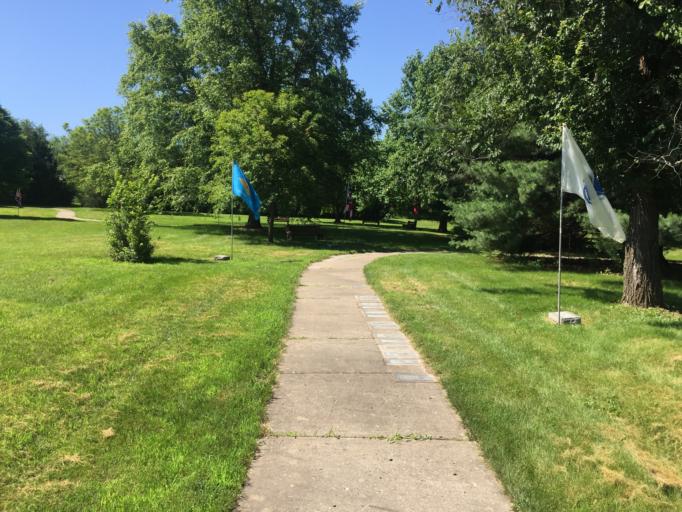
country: US
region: Kansas
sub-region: Atchison County
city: Atchison
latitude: 39.5324
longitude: -95.1495
